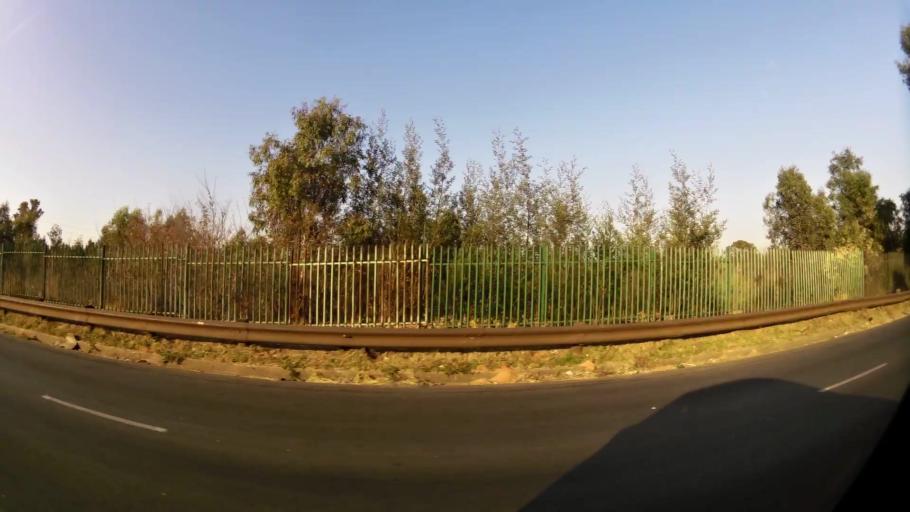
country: ZA
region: Gauteng
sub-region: City of Johannesburg Metropolitan Municipality
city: Johannesburg
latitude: -26.2107
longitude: 27.9928
